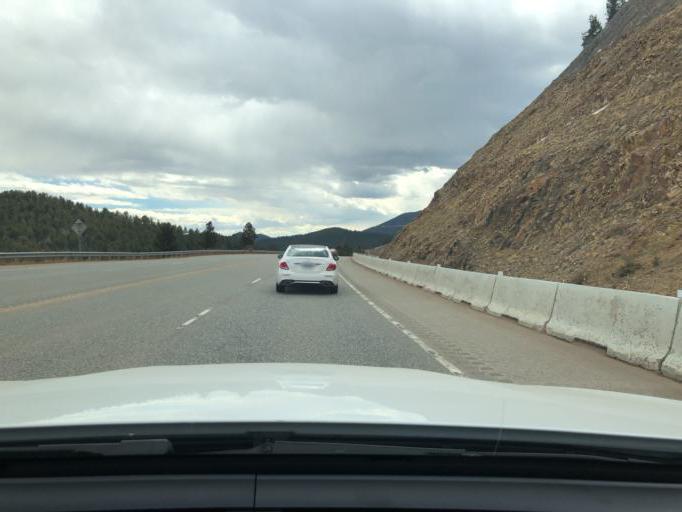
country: US
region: Colorado
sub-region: Gilpin County
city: Central City
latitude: 39.7774
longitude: -105.4755
